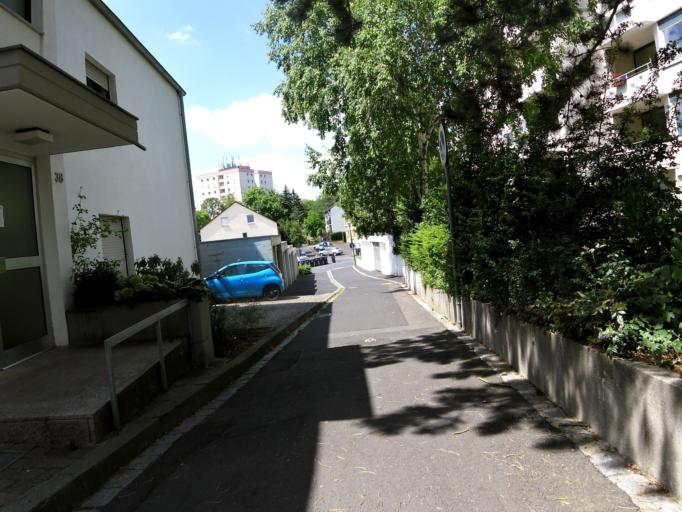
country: DE
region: Bavaria
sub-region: Regierungsbezirk Unterfranken
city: Gerbrunn
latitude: 49.7805
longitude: 9.9881
